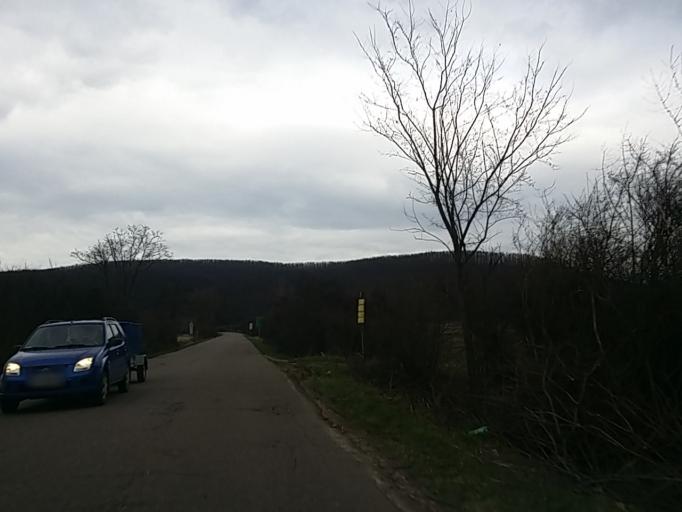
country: HU
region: Heves
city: Sirok
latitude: 47.9171
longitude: 20.1773
